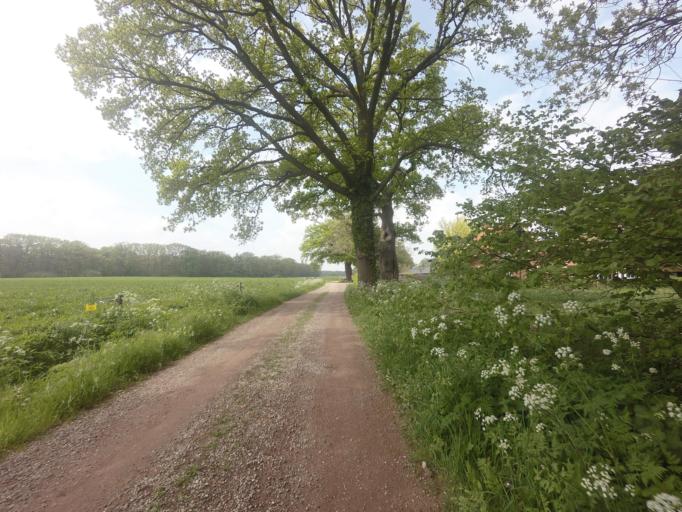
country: NL
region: Overijssel
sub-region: Gemeente Hof van Twente
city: Delden
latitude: 52.2136
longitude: 6.7297
